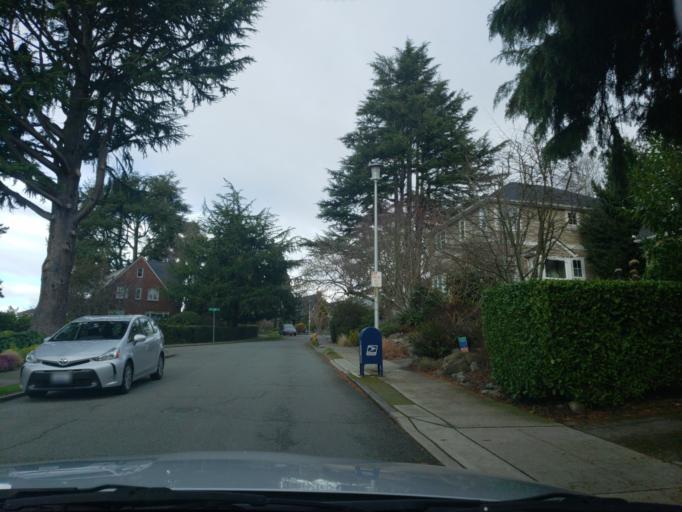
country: US
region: Washington
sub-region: King County
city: Medina
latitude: 47.6551
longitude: -122.2770
